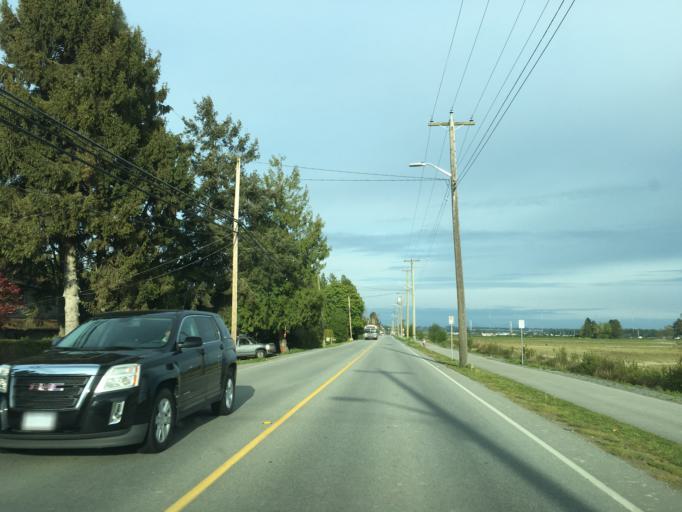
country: CA
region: British Columbia
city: Ladner
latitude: 49.1699
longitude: -123.0332
